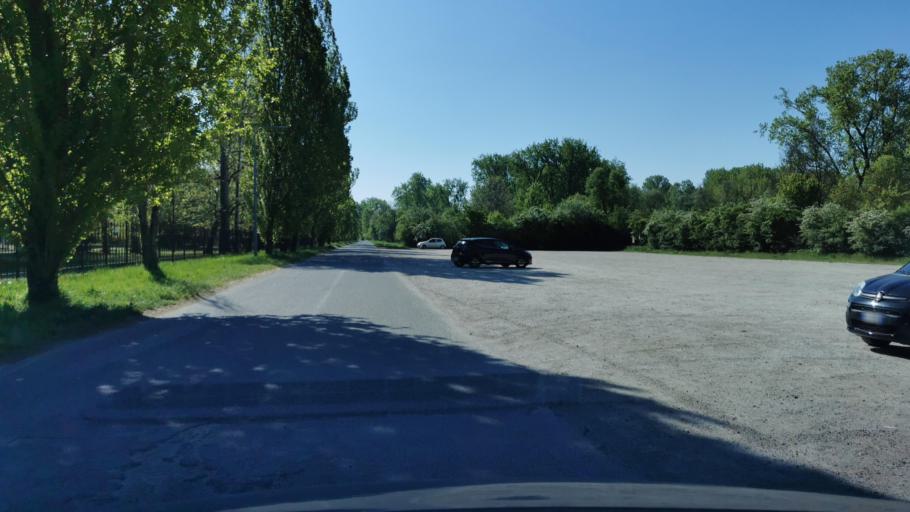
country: IT
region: Lombardy
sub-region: Provincia di Cremona
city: Cremona
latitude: 45.1228
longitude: 10.0053
